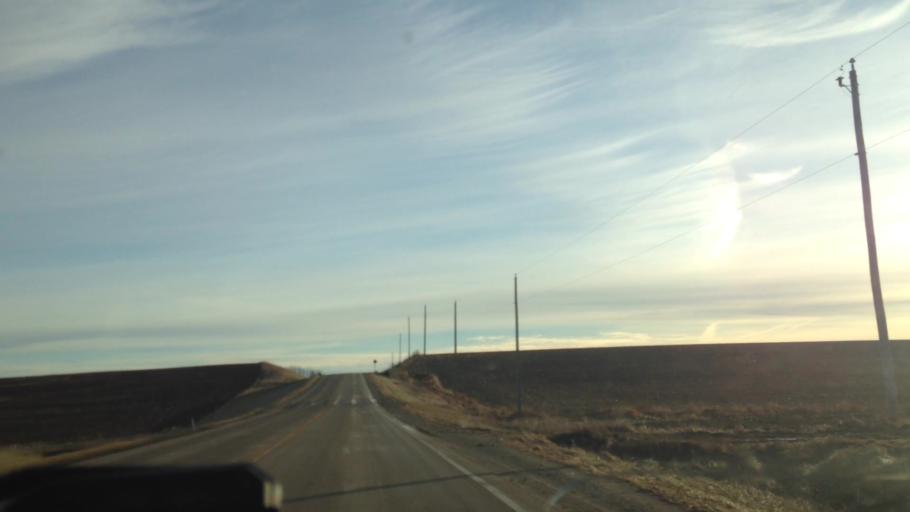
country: US
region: Wisconsin
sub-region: Dodge County
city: Theresa
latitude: 43.5363
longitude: -88.4608
